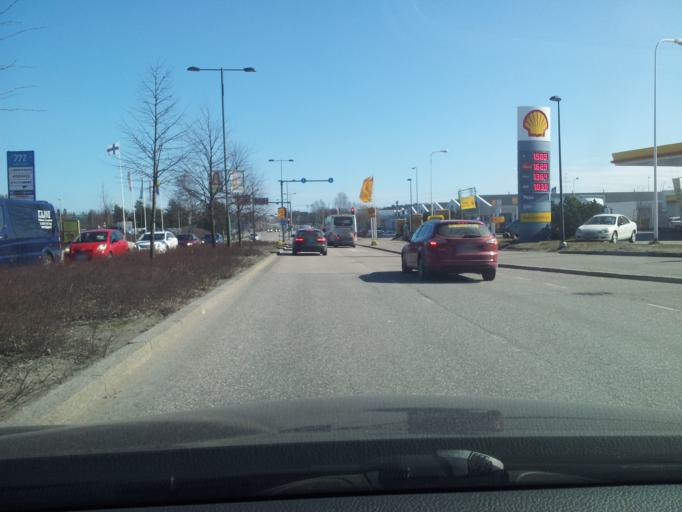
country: FI
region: Uusimaa
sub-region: Helsinki
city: Kauniainen
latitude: 60.1619
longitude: 24.7055
